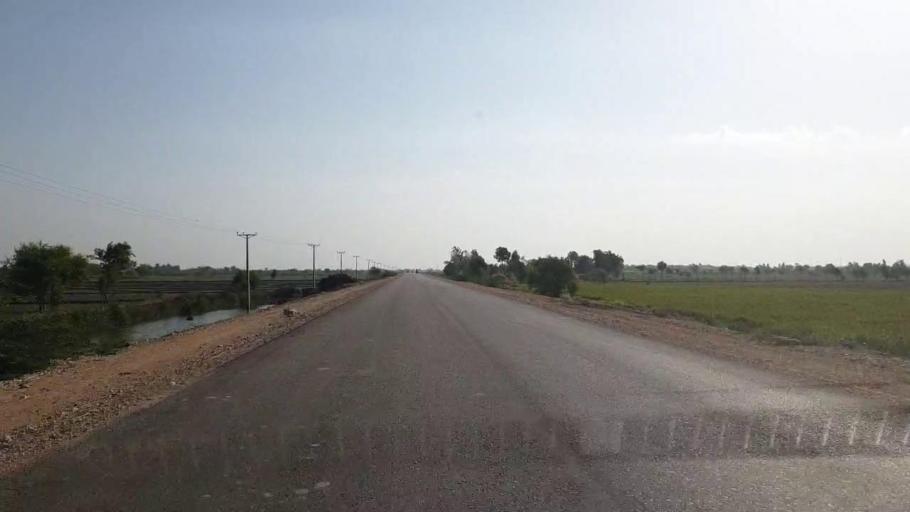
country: PK
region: Sindh
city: Tando Bago
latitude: 24.6571
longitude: 69.0094
